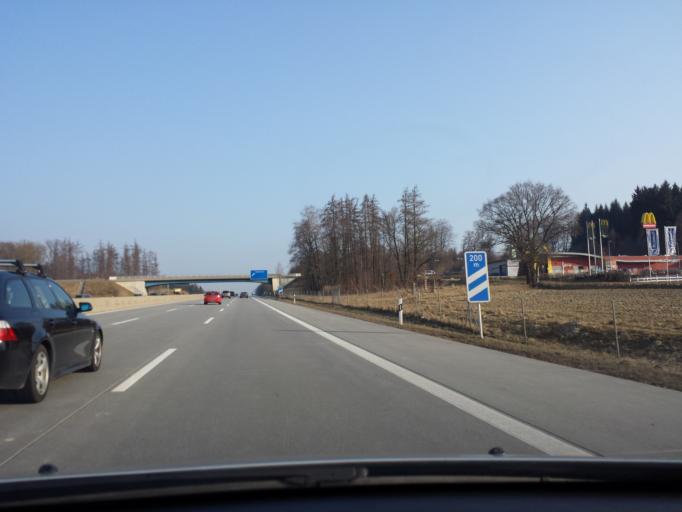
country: DE
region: Bavaria
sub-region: Upper Bavaria
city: Sulzemoos
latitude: 48.2819
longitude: 11.2672
